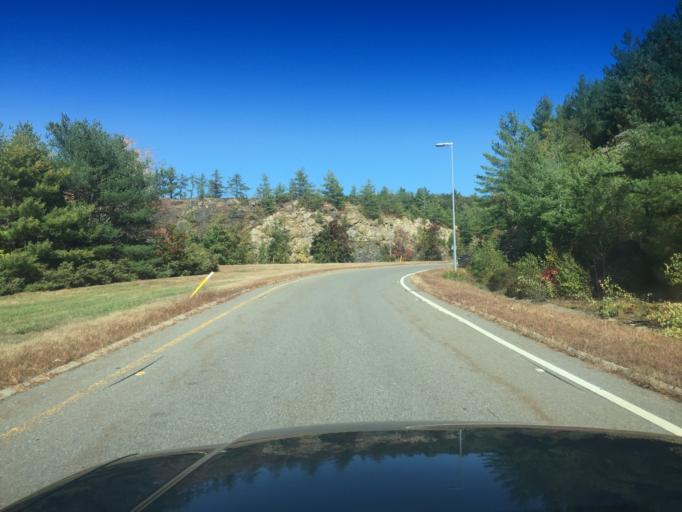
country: US
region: Massachusetts
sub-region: Middlesex County
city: Hudson
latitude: 42.3626
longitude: -71.5862
